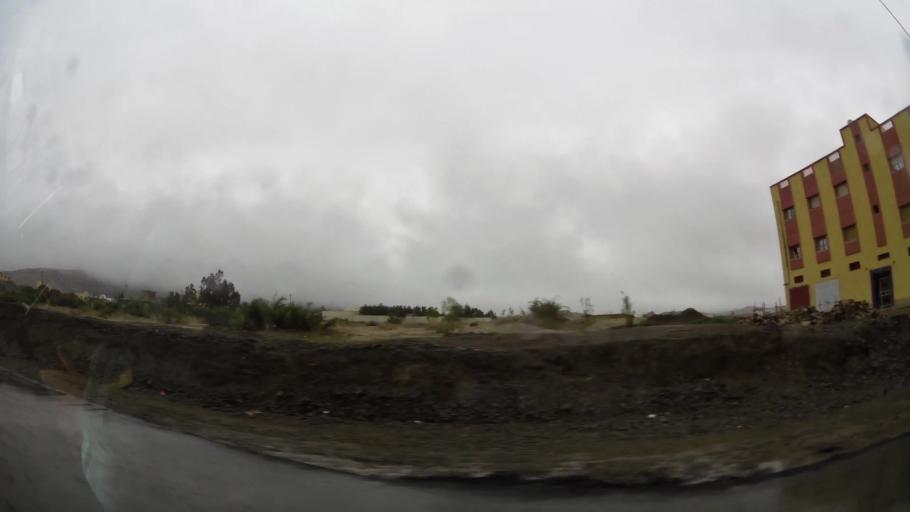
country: MA
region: Taza-Al Hoceima-Taounate
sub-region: Taza
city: Aknoul
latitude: 34.8154
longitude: -3.7307
